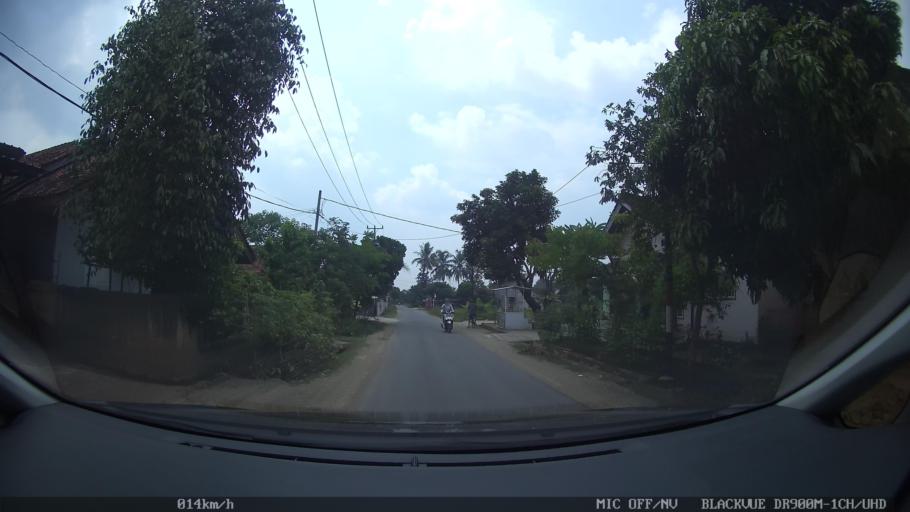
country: ID
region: Lampung
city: Gadingrejo
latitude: -5.3848
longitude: 105.0424
